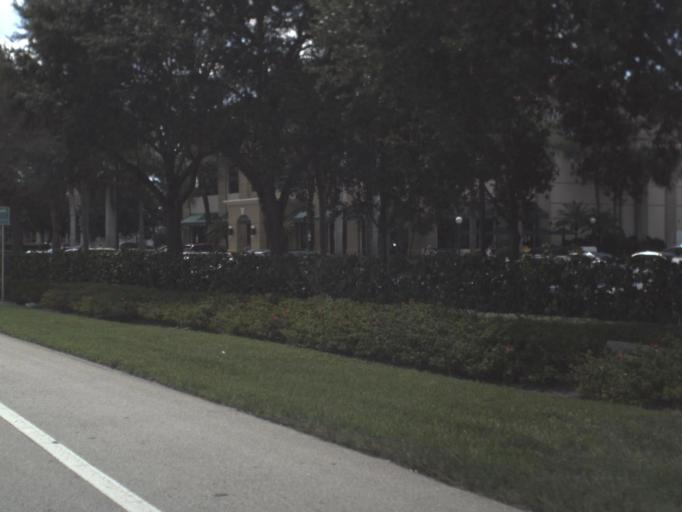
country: US
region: Florida
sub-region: Collier County
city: Pine Ridge
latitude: 26.2125
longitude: -81.8006
